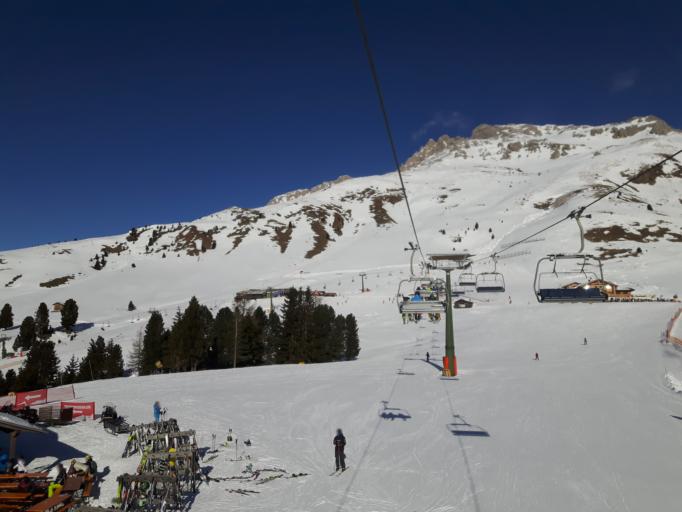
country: IT
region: Trentino-Alto Adige
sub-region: Provincia di Trento
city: Panchia
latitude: 46.3479
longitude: 11.5454
